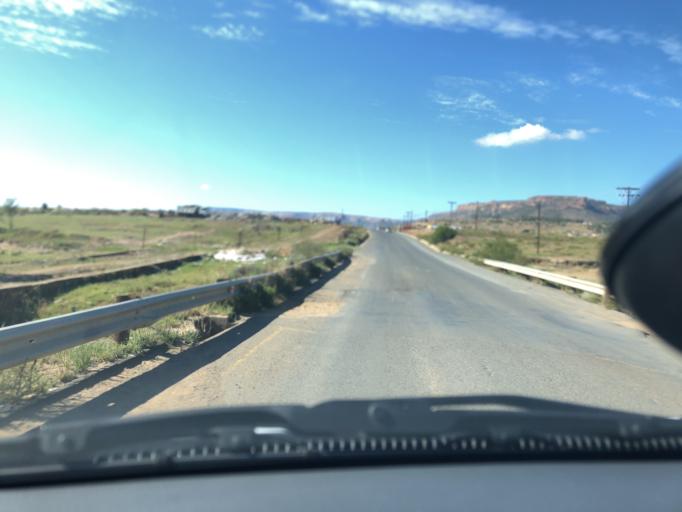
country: LS
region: Maseru
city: Maseru
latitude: -29.3770
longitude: 27.4705
